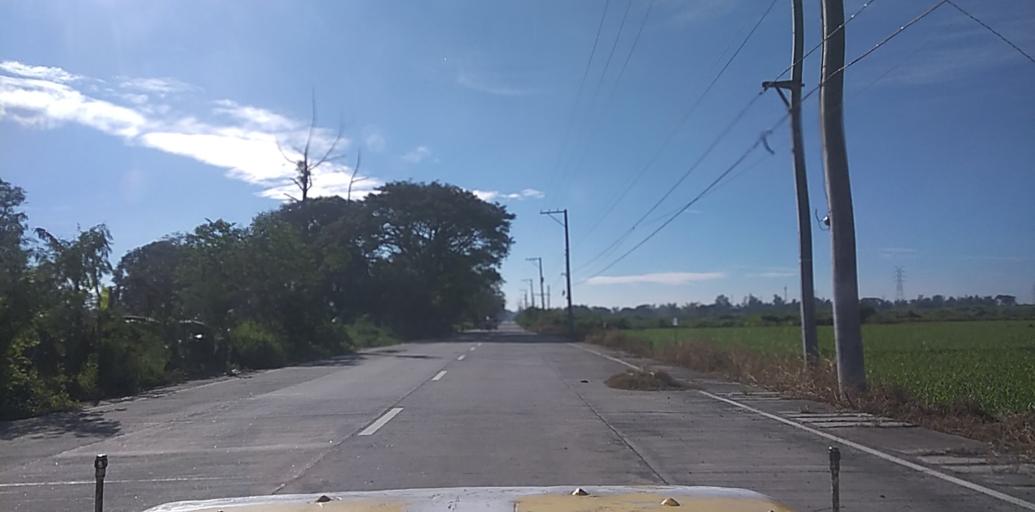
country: PH
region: Central Luzon
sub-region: Province of Pampanga
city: Anao
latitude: 15.1305
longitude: 120.6973
